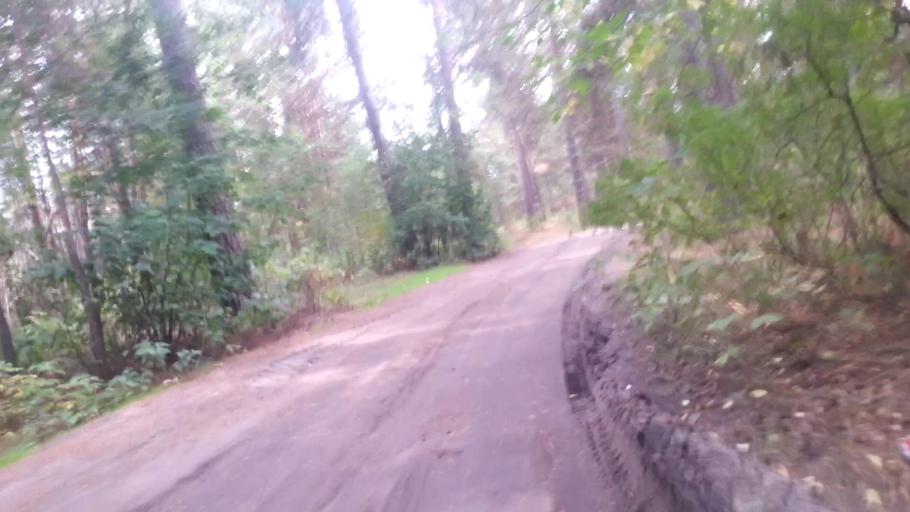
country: RU
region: Altai Krai
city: Yuzhnyy
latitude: 53.3094
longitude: 83.6988
